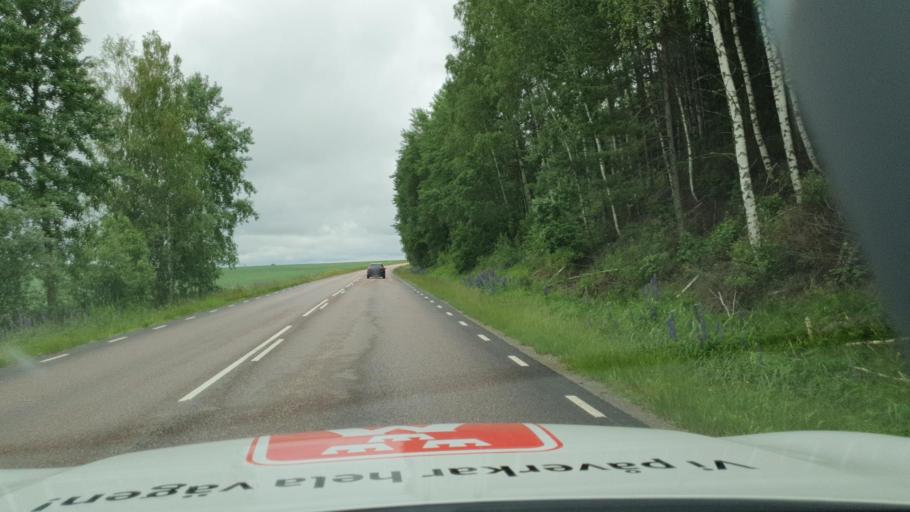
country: SE
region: Vaermland
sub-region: Karlstads Kommun
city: Edsvalla
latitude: 59.4065
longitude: 13.2106
